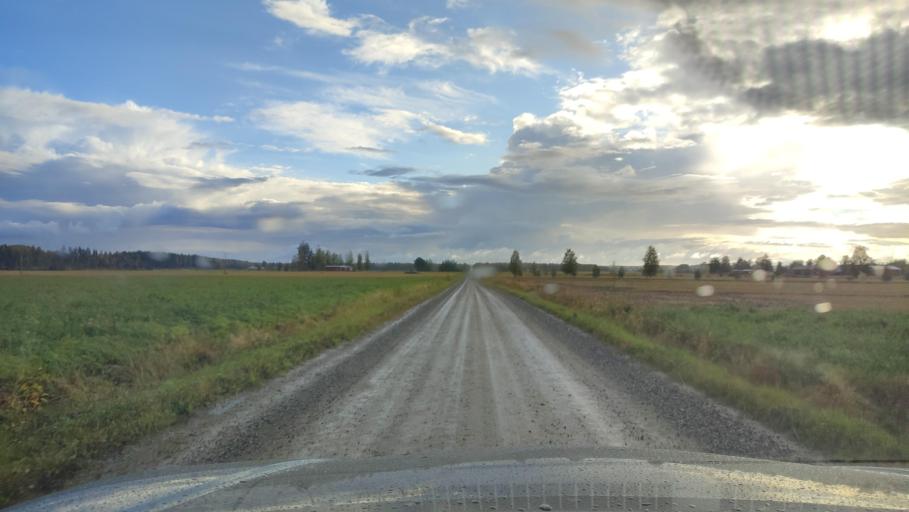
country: FI
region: Southern Ostrobothnia
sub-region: Suupohja
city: Karijoki
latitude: 62.3323
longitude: 21.5864
